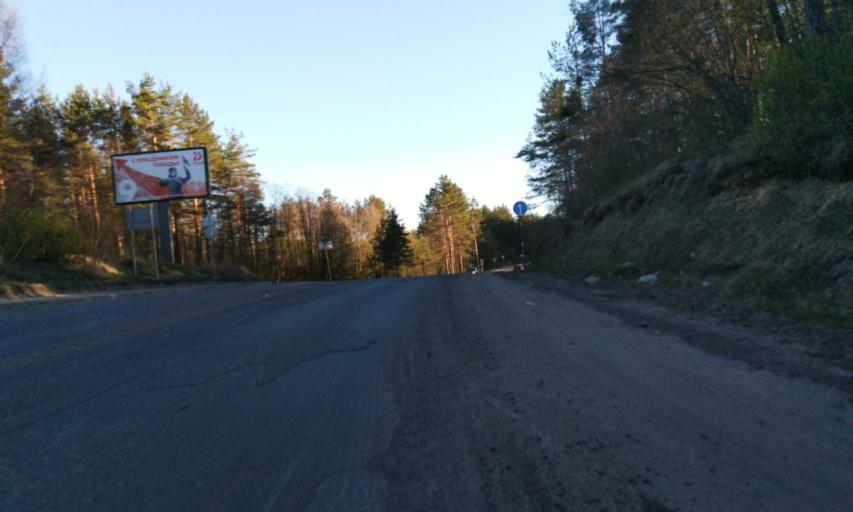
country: RU
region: Leningrad
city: Toksovo
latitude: 60.1347
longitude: 30.5274
